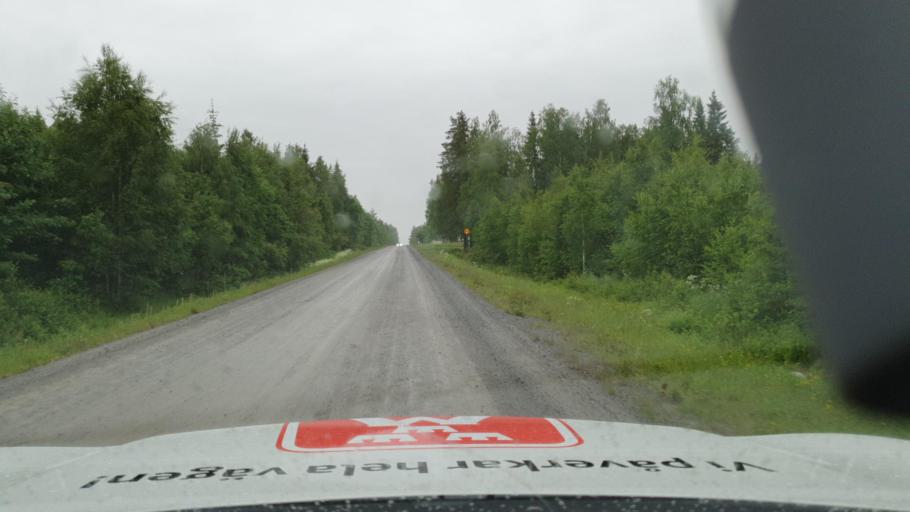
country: SE
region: Vaesterbotten
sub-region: Bjurholms Kommun
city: Bjurholm
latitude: 63.8562
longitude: 19.4716
